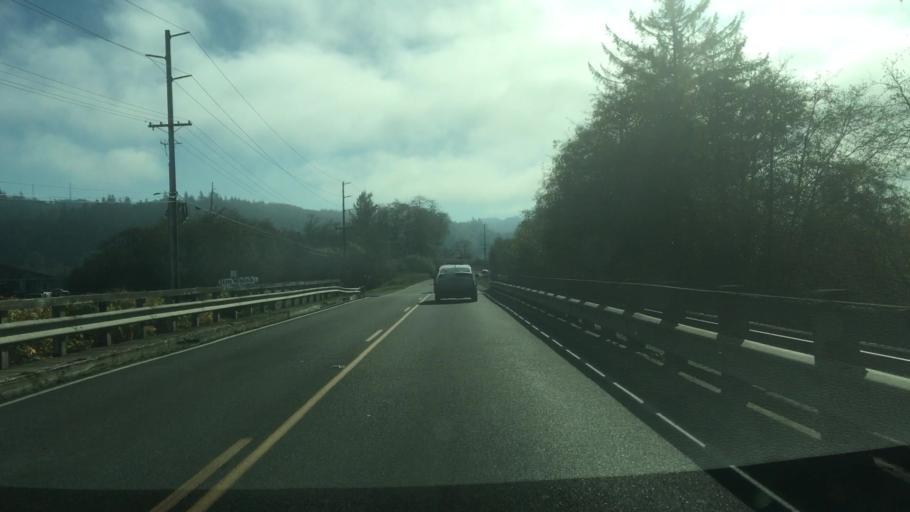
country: US
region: Washington
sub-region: Grays Harbor County
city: Montesano
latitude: 46.9734
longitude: -123.6010
